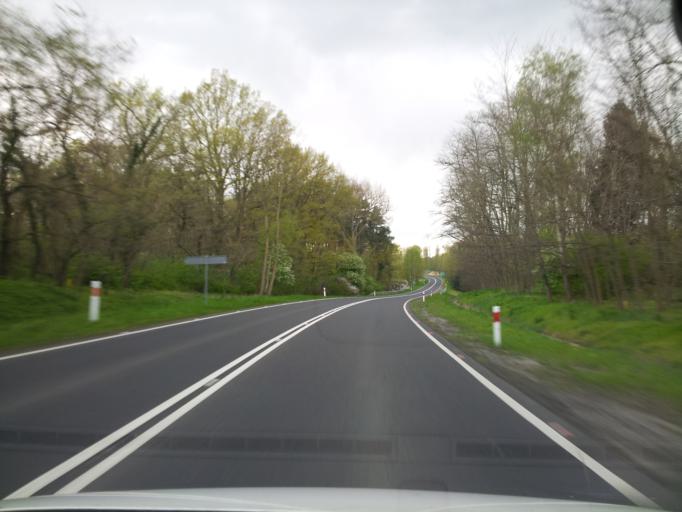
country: PL
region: Lubusz
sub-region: Powiat krosnienski
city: Krosno Odrzanskie
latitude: 52.0126
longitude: 15.0763
